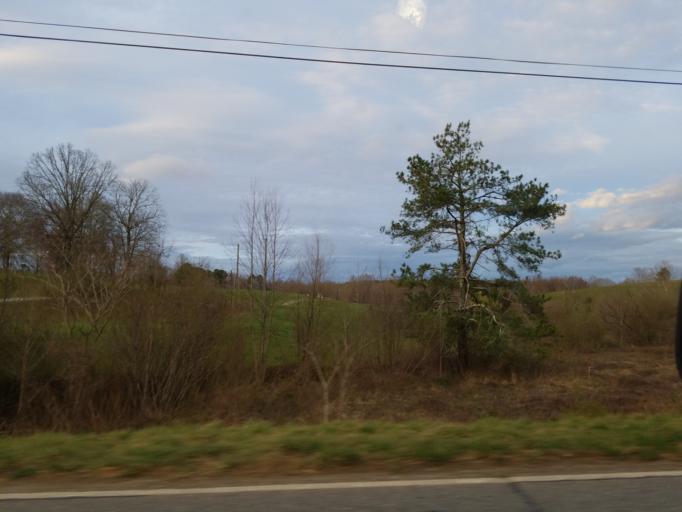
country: US
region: Georgia
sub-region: Pickens County
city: Jasper
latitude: 34.4684
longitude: -84.4951
